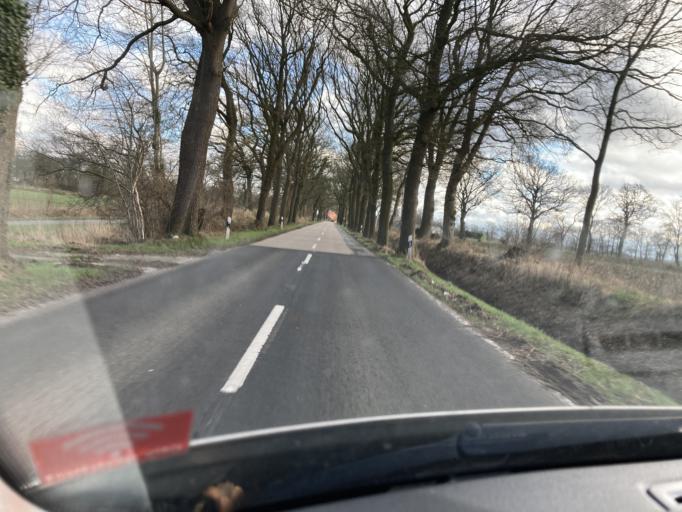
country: DE
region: Lower Saxony
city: Filsum
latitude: 53.2389
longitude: 7.6486
